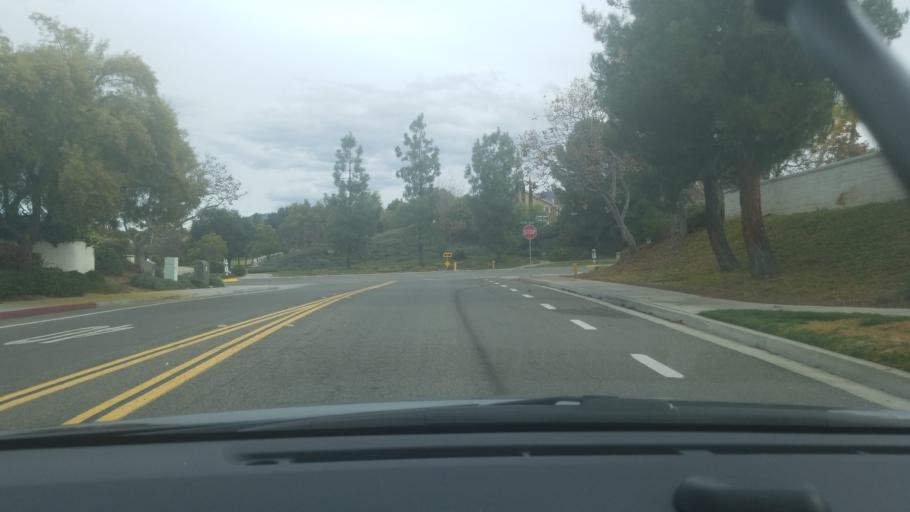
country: US
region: California
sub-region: Riverside County
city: Temecula
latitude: 33.4779
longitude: -117.0875
